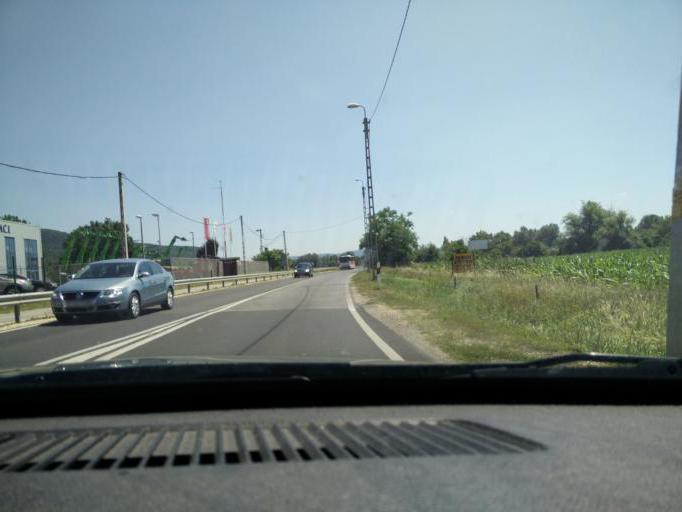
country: HU
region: Komarom-Esztergom
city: Vertesszolos
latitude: 47.6120
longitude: 18.3830
